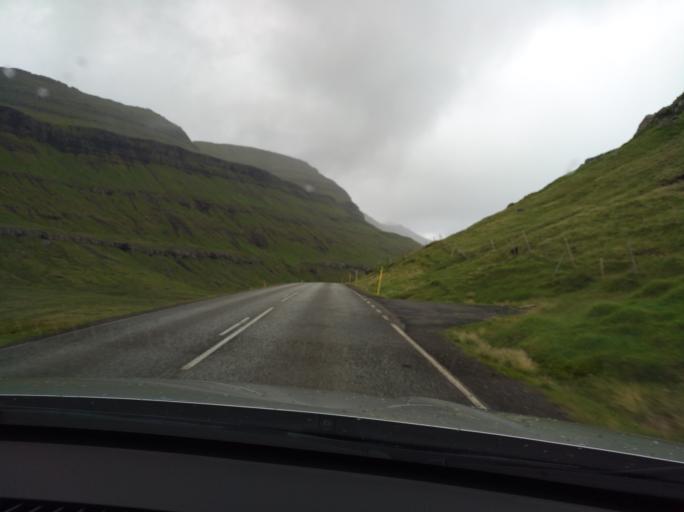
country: FO
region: Eysturoy
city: Fuglafjordur
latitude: 62.2309
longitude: -6.8798
